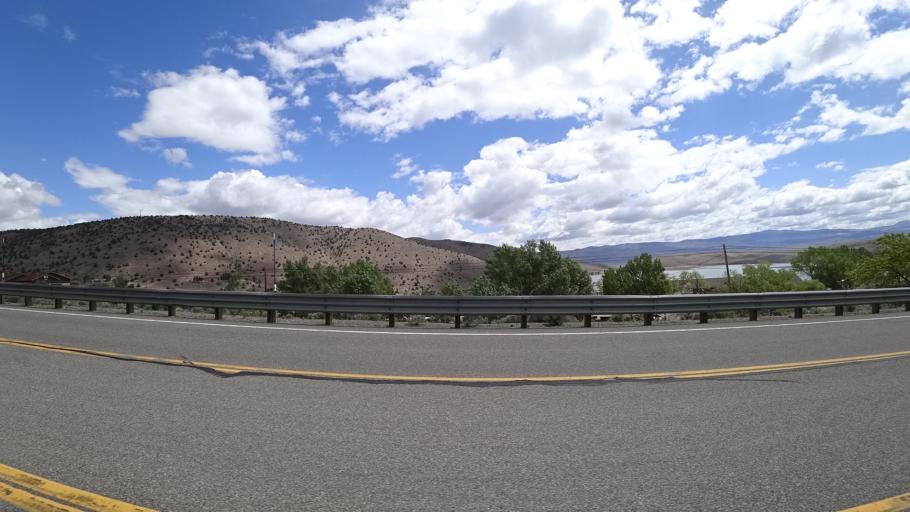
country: US
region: Nevada
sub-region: Lyon County
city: Smith Valley
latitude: 38.6975
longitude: -119.5495
